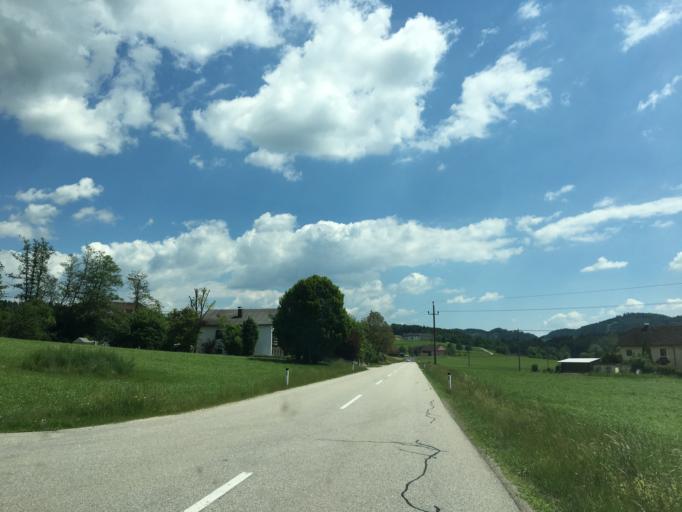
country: AT
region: Upper Austria
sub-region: Politischer Bezirk Perg
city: Perg
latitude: 48.3198
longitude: 14.5999
